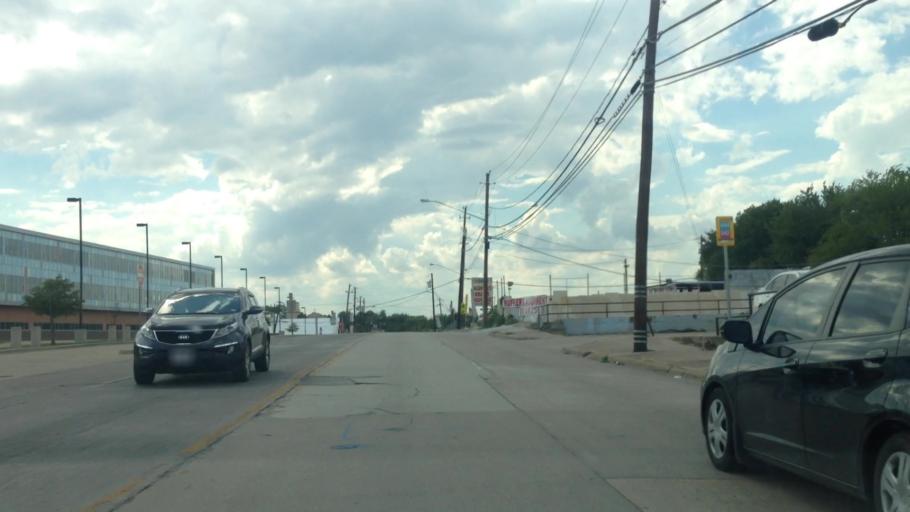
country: US
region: Texas
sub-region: Dallas County
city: Dallas
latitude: 32.7513
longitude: -96.8128
